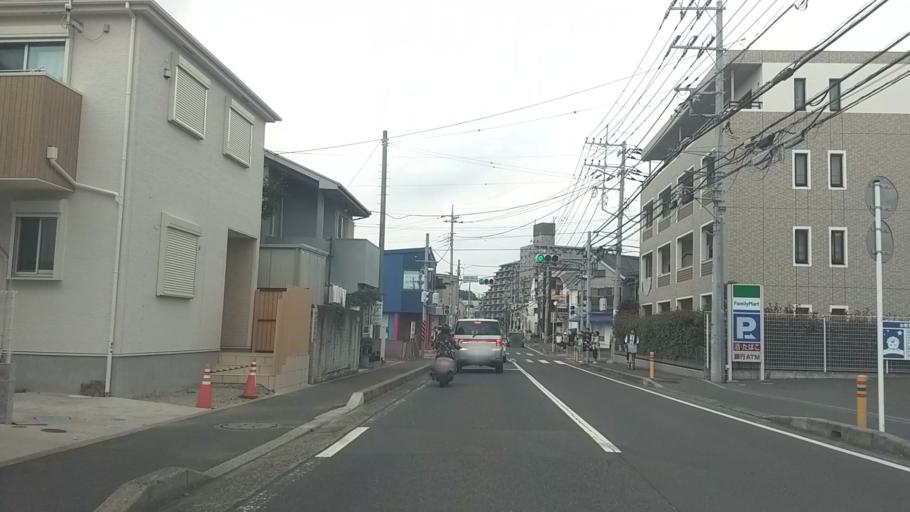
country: JP
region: Kanagawa
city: Fujisawa
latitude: 35.3428
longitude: 139.4371
